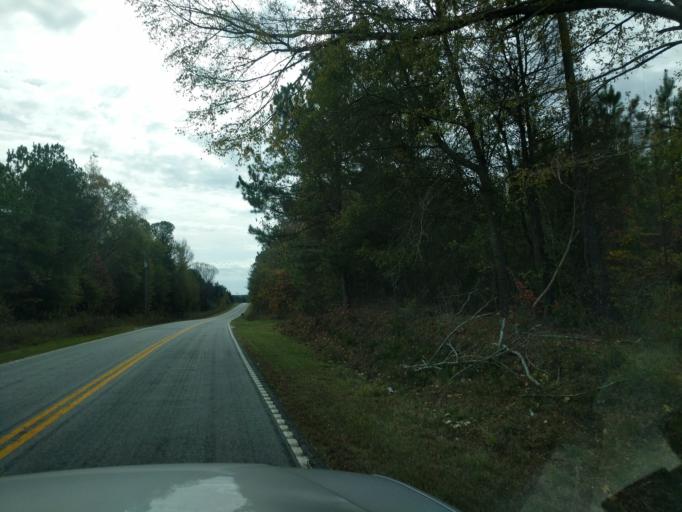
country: US
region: South Carolina
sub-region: Laurens County
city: Joanna
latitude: 34.3509
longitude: -81.8571
